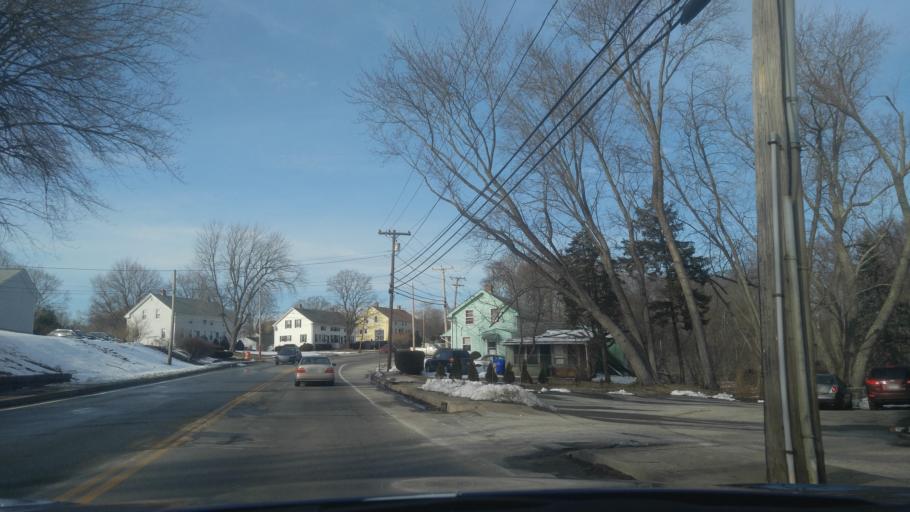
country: US
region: Rhode Island
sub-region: Kent County
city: West Warwick
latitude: 41.7249
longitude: -71.4915
